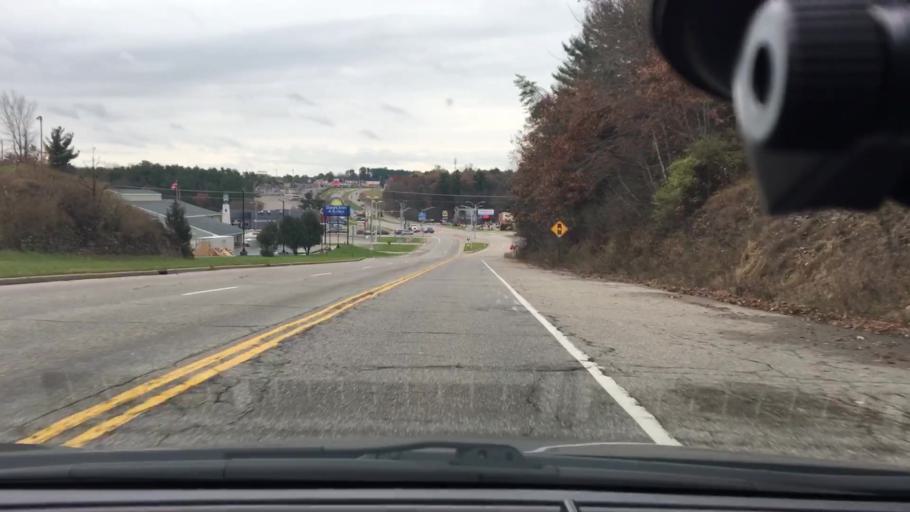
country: US
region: Wisconsin
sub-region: Columbia County
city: Wisconsin Dells
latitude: 43.6288
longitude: -89.7871
